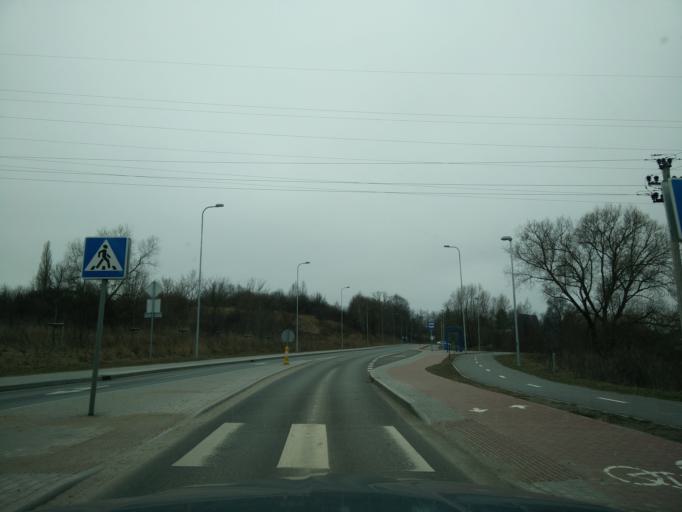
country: LT
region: Klaipedos apskritis
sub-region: Klaipeda
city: Klaipeda
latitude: 55.7181
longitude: 21.1687
